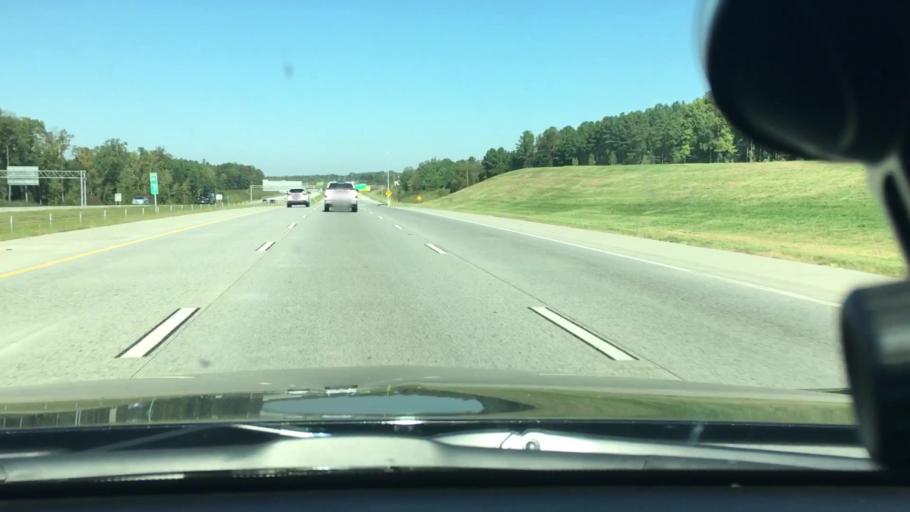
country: US
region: North Carolina
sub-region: Cabarrus County
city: Harrisburg
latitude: 35.3514
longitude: -80.7359
